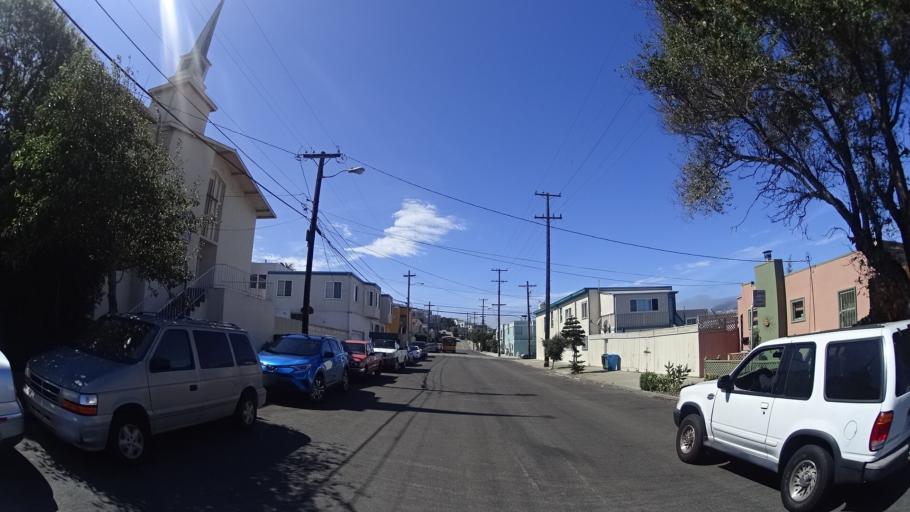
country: US
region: California
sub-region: San Francisco County
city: San Francisco
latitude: 37.7285
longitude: -122.4209
